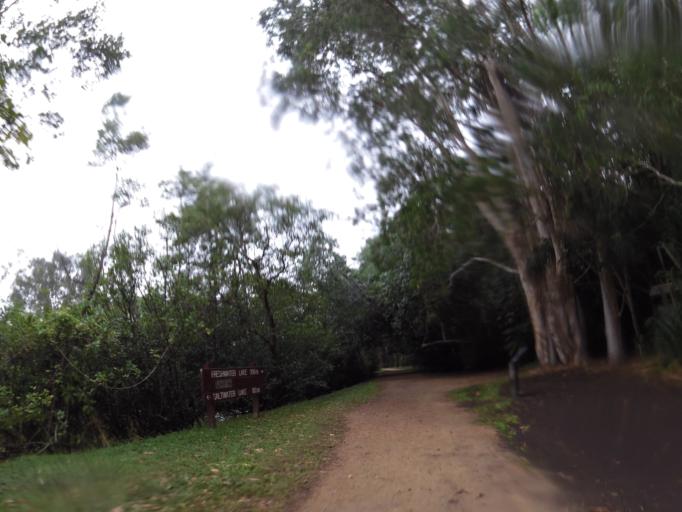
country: AU
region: Queensland
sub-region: Cairns
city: Cairns
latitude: -16.9012
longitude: 145.7514
